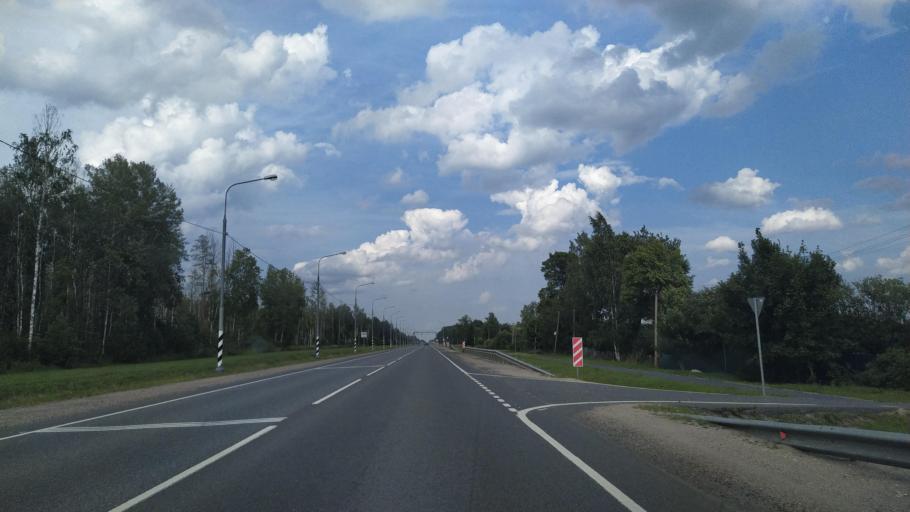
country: RU
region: Novgorod
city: Shimsk
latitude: 58.2574
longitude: 30.8023
